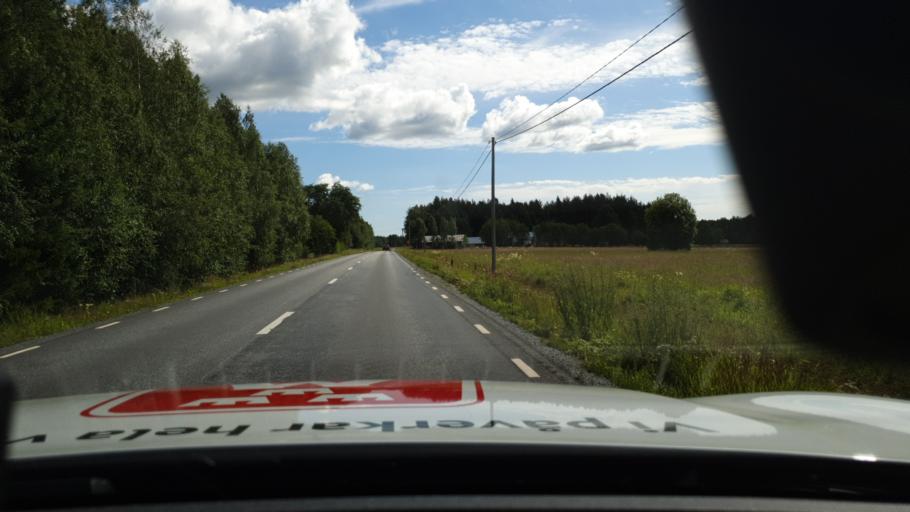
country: SE
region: Norrbotten
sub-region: Lulea Kommun
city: Gammelstad
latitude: 65.8005
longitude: 22.0527
